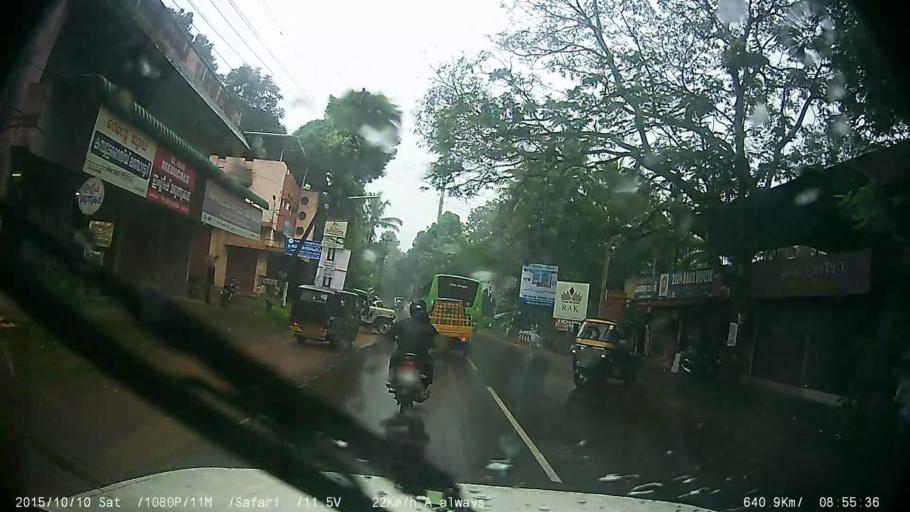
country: IN
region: Kerala
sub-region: Kottayam
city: Palackattumala
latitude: 9.6989
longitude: 76.5490
